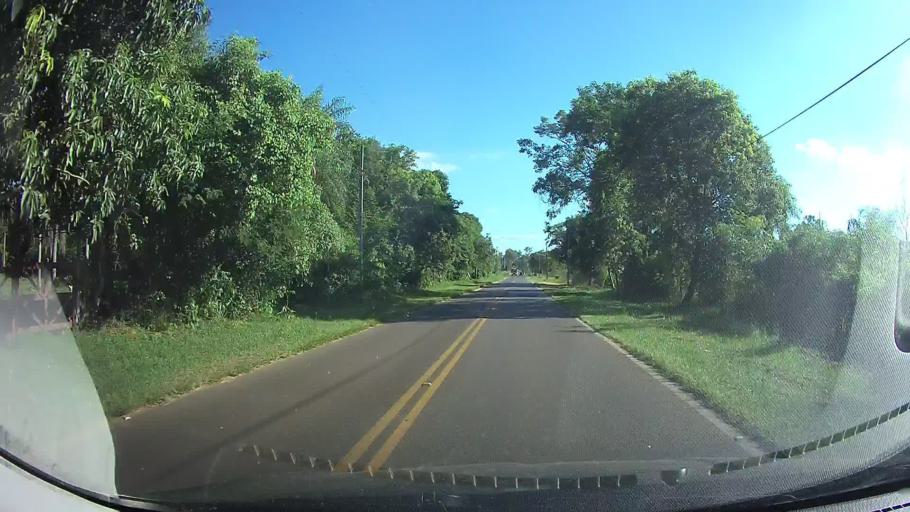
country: PY
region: Cordillera
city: Atyra
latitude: -25.2963
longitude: -57.1848
